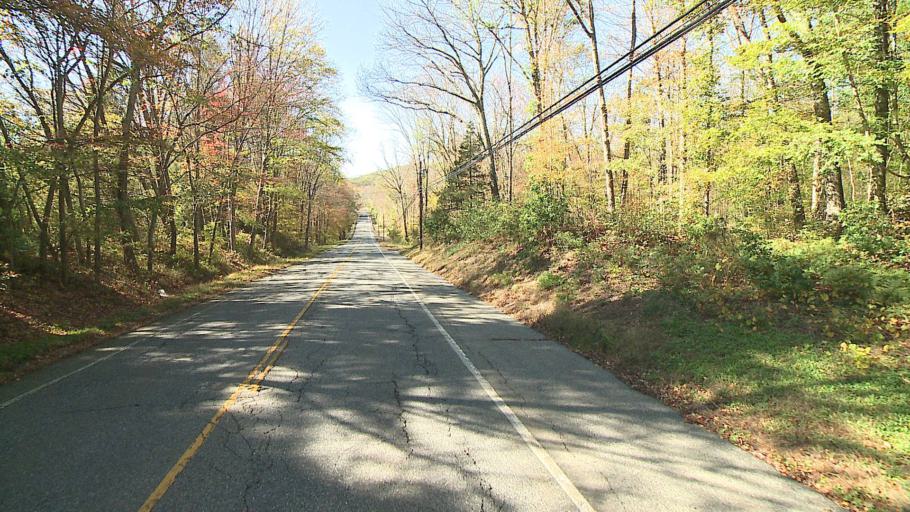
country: US
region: Connecticut
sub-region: Hartford County
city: Terramuggus
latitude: 41.6456
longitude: -72.4328
